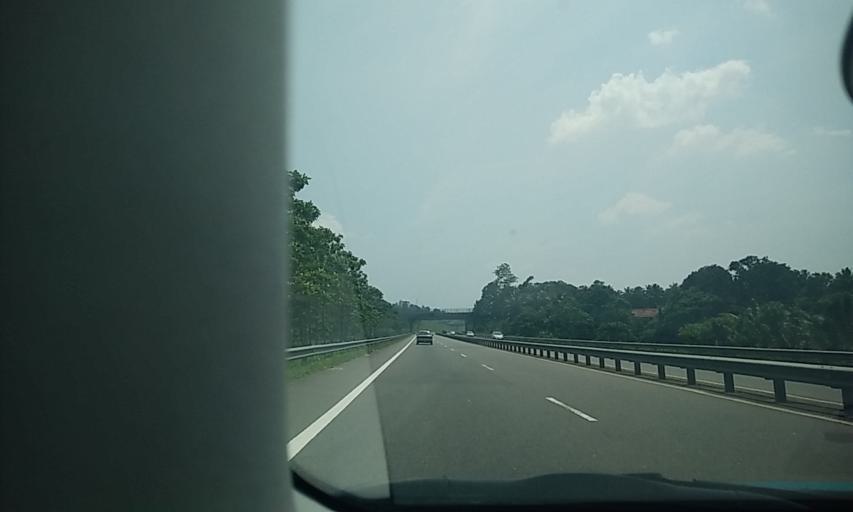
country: LK
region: Western
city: Horana South
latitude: 6.7551
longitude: 79.9931
